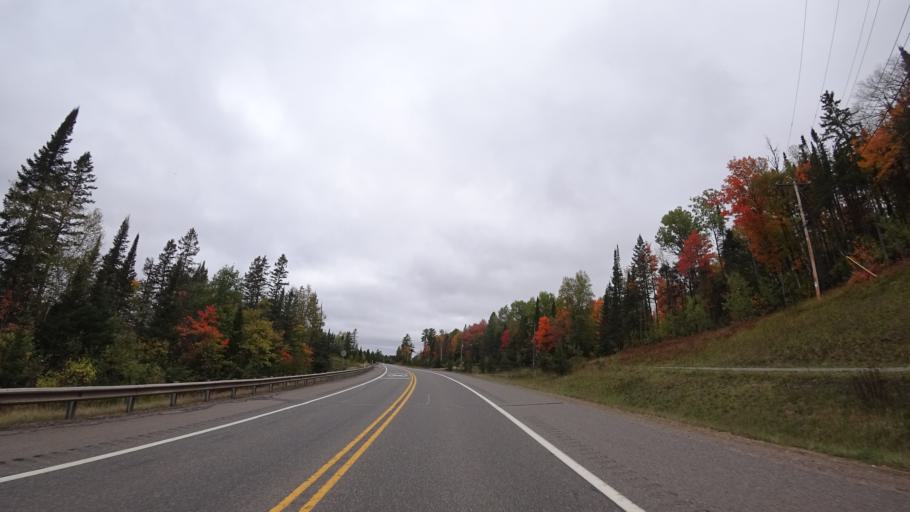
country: US
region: Michigan
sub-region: Marquette County
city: West Ishpeming
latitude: 46.5174
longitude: -87.9749
